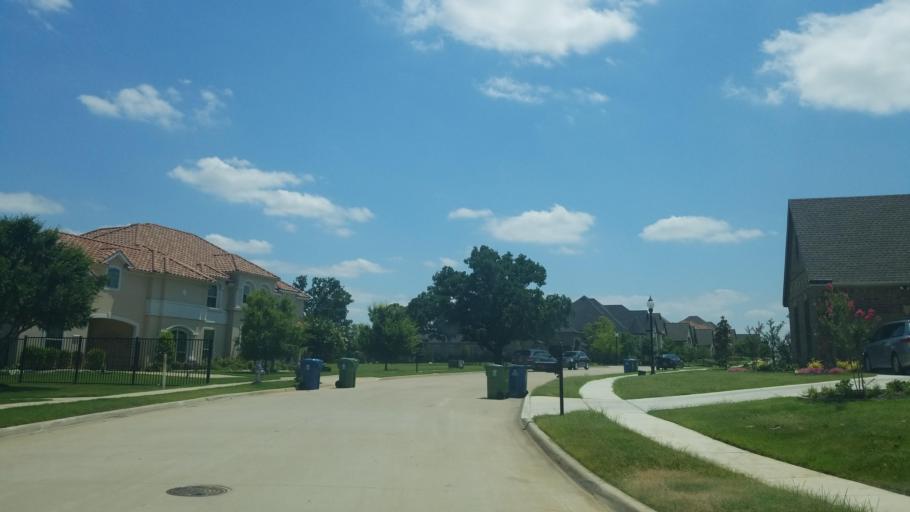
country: US
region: Texas
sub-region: Denton County
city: Copper Canyon
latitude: 33.0778
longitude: -97.0873
